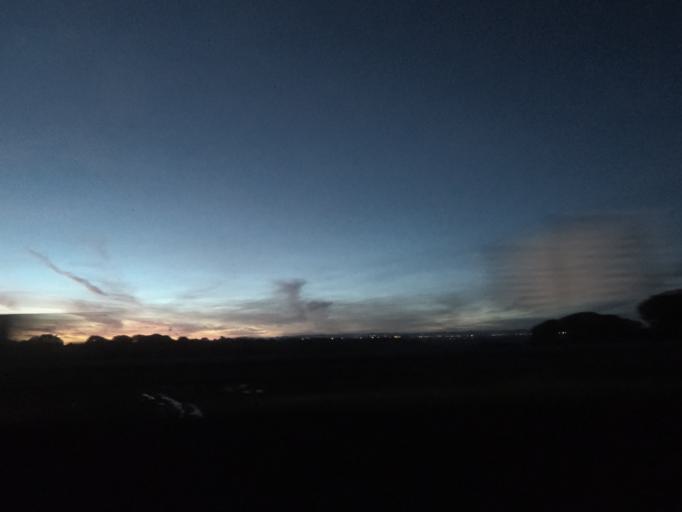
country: PT
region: Santarem
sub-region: Benavente
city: Benavente
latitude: 38.9377
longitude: -8.8194
